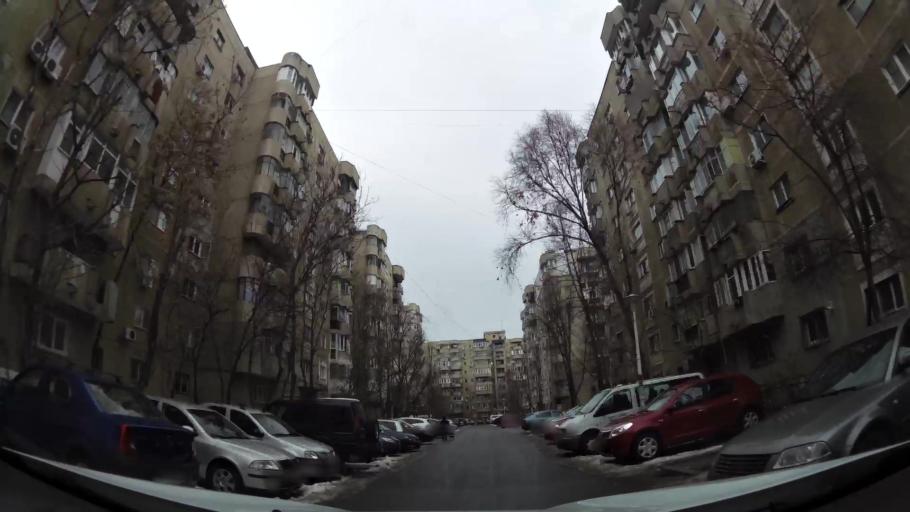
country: RO
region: Bucuresti
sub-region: Municipiul Bucuresti
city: Bucuresti
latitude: 44.4180
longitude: 26.0647
